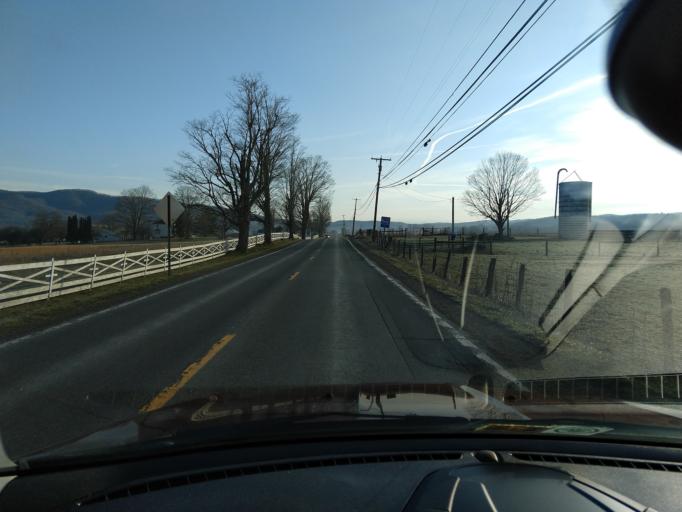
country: US
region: West Virginia
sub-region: Pocahontas County
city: Marlinton
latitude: 38.1401
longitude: -80.2055
